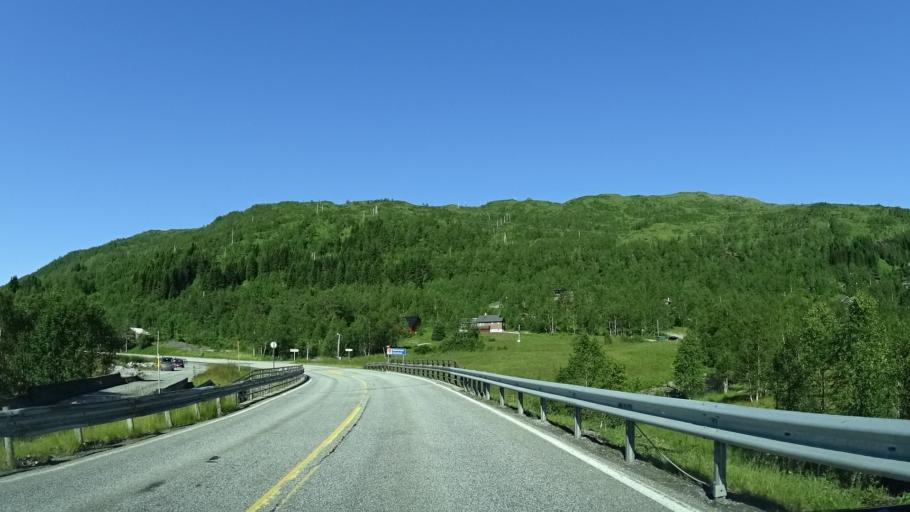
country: NO
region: Hordaland
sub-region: Samnanger
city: Tysse
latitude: 60.3968
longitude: 5.9180
